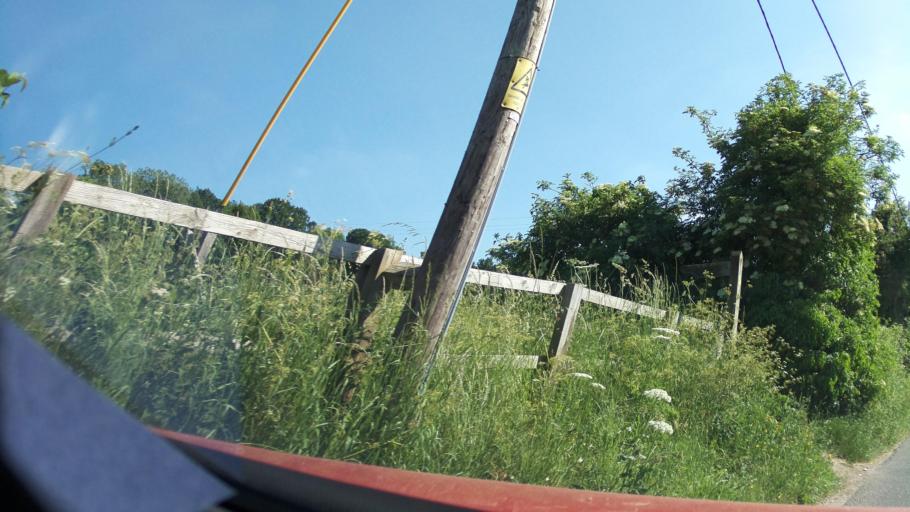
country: GB
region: England
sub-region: Hampshire
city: Abbotts Ann
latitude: 51.2325
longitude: -1.5630
